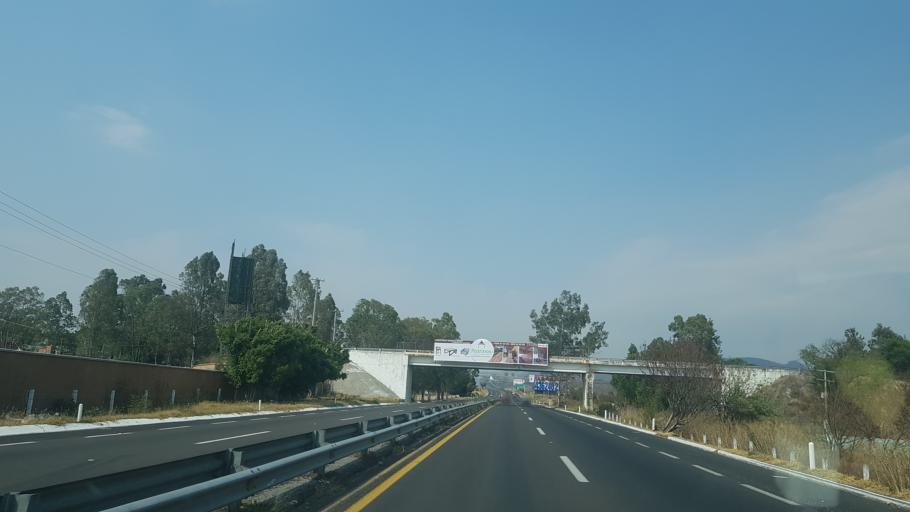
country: MX
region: Puebla
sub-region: Atlixco
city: San Agustin Huixaxtla
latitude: 18.9277
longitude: -98.3982
